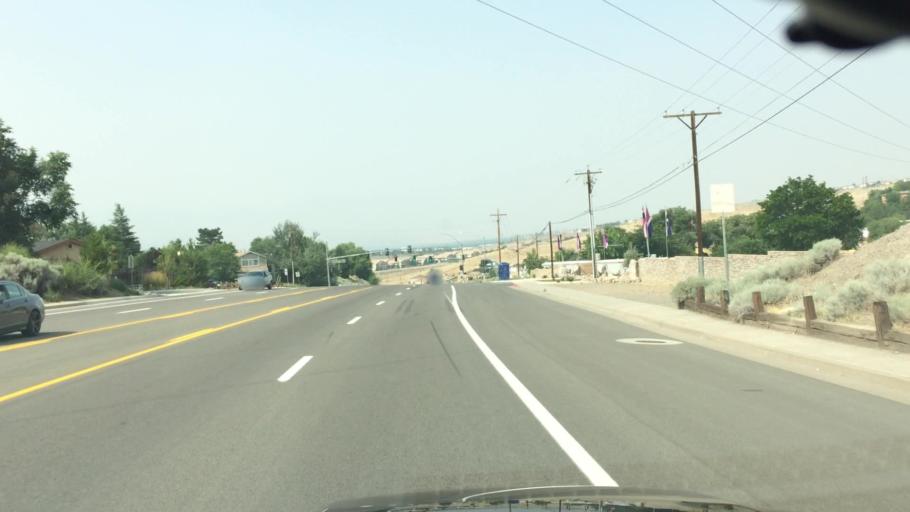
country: US
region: Nevada
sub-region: Washoe County
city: Sun Valley
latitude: 39.5648
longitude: -119.7847
